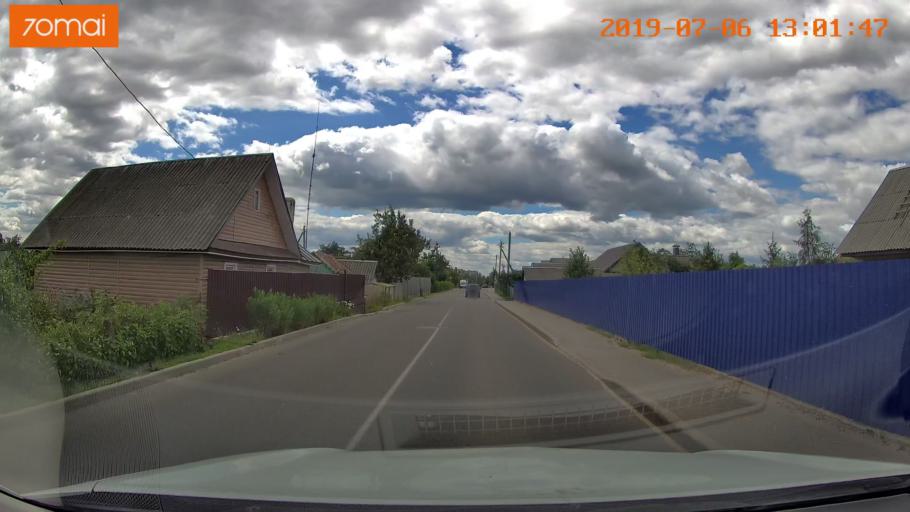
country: BY
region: Minsk
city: Dzyarzhynsk
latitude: 53.6889
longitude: 27.1216
